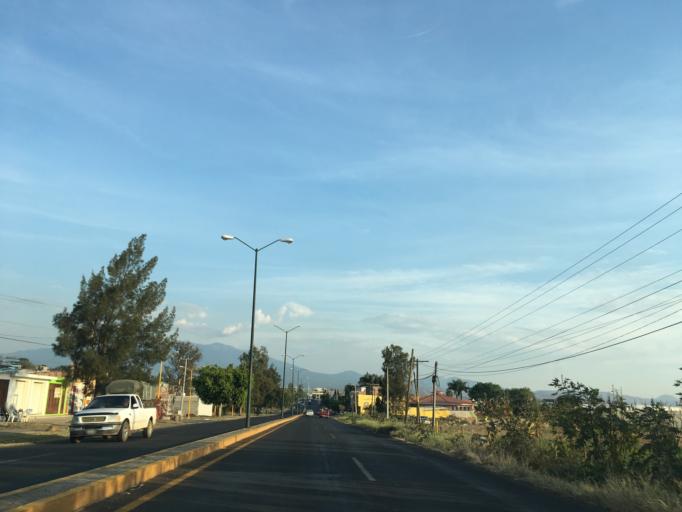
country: MX
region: Michoacan
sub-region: Los Reyes
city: La Higuerita (Colonia San Rafael)
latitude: 19.6080
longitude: -102.4798
